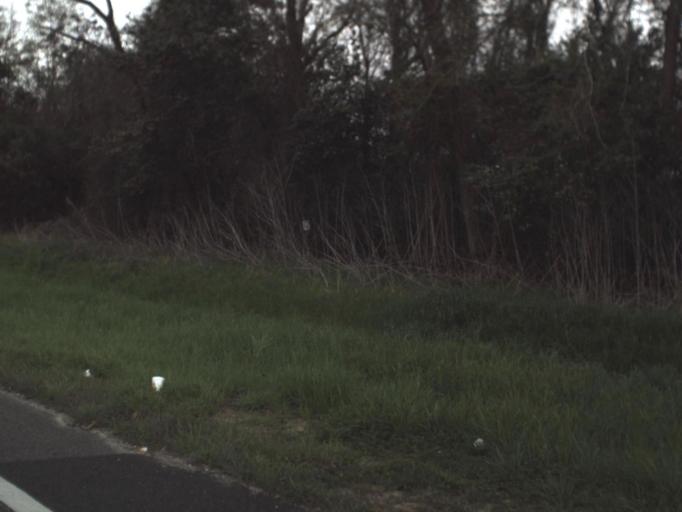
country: US
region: Florida
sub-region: Leon County
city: Tallahassee
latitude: 30.4282
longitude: -84.1914
